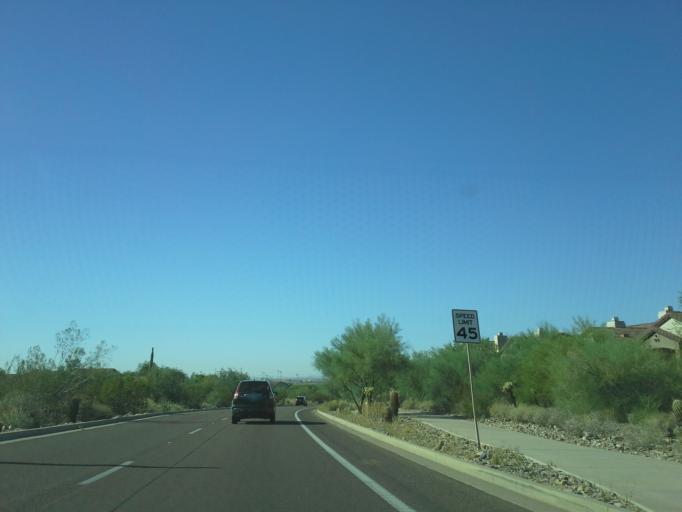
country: US
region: Arizona
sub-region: Maricopa County
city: Scottsdale
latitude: 33.6329
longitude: -111.8606
